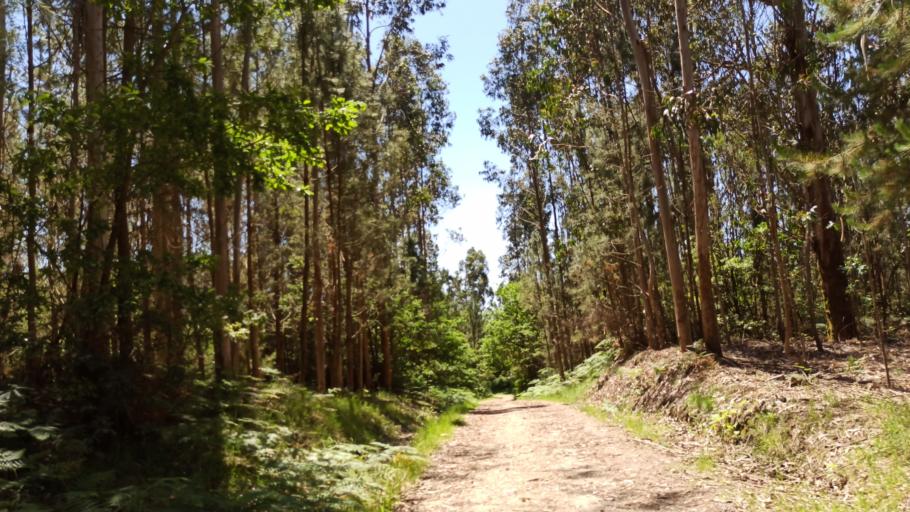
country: ES
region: Galicia
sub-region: Provincia da Coruna
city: Negreira
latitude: 42.9194
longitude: -8.7199
